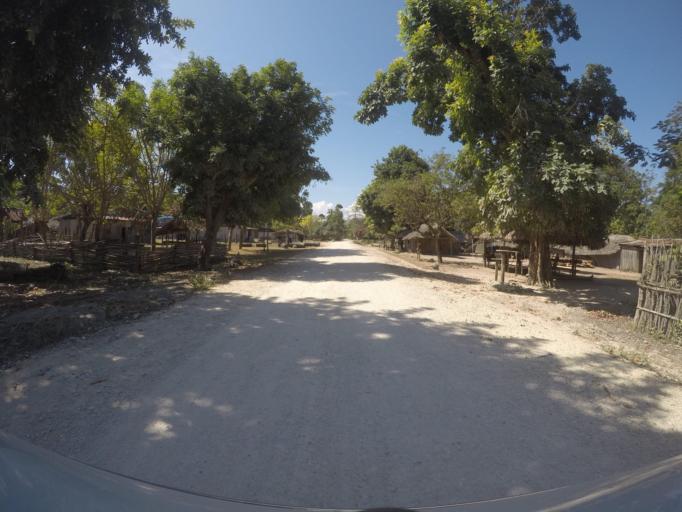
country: TL
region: Viqueque
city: Viqueque
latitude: -8.9054
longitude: 126.5054
